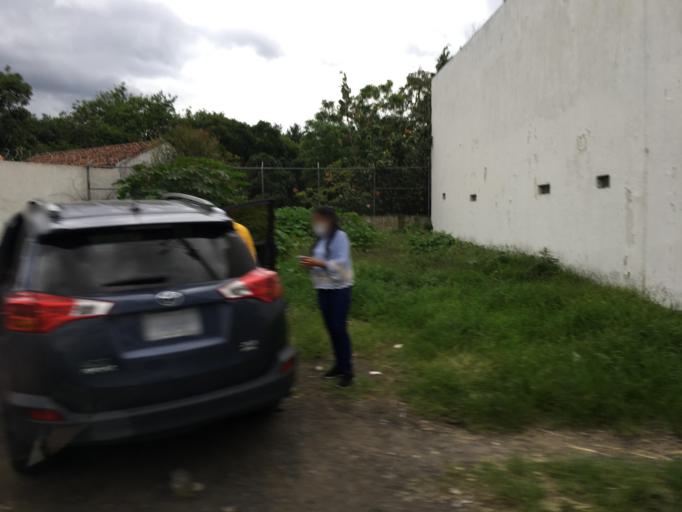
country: GT
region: Sacatepequez
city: Antigua Guatemala
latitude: 14.5677
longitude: -90.7367
